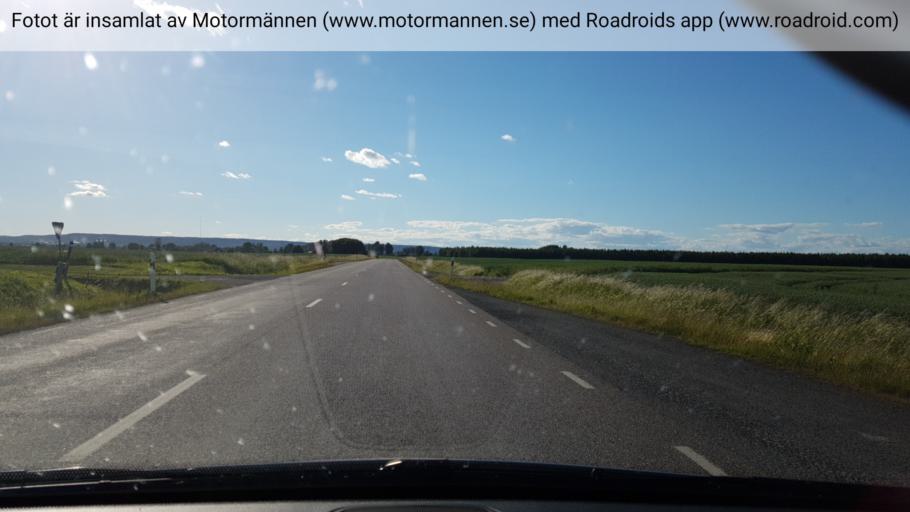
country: SE
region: Vaestra Goetaland
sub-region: Skovde Kommun
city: Skoevde
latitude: 58.3780
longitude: 13.9739
